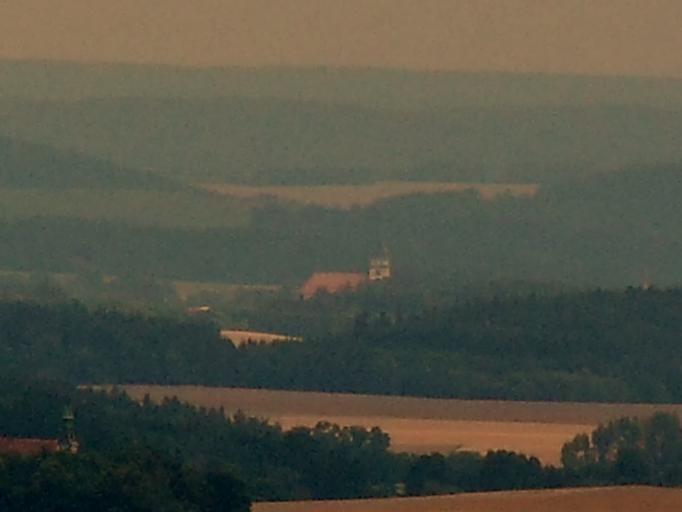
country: CZ
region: Vysocina
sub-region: Okres Jihlava
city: Trest'
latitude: 49.2520
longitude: 15.4265
